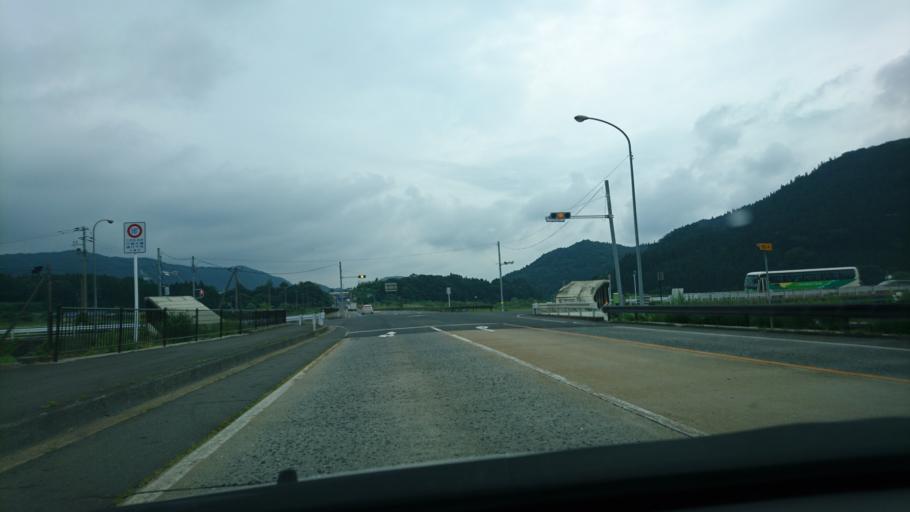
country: JP
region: Miyagi
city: Furukawa
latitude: 38.7347
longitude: 140.7686
